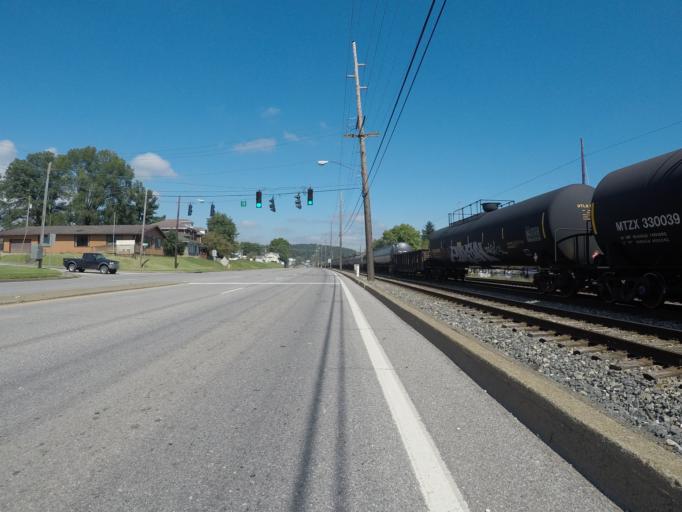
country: US
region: Ohio
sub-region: Lawrence County
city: South Point
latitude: 38.4424
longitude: -82.6098
